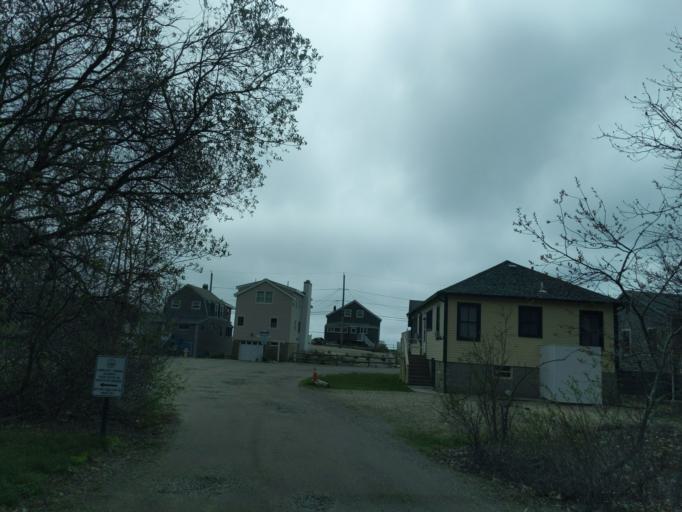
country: US
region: Massachusetts
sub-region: Essex County
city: Rockport
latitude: 42.6281
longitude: -70.6211
